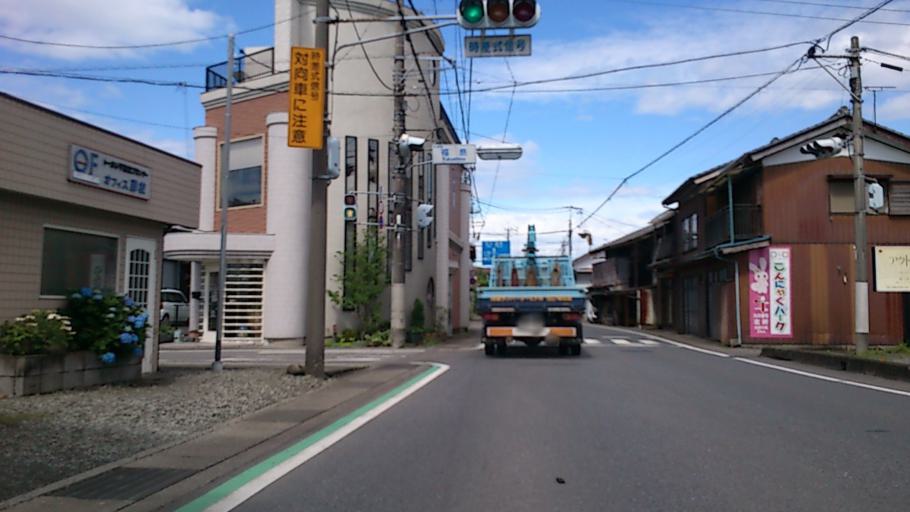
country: JP
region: Gunma
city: Tomioka
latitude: 36.2543
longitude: 138.9313
